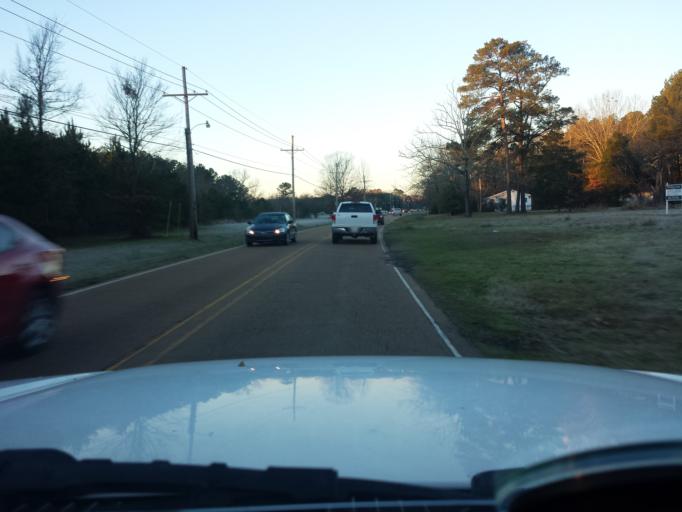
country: US
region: Mississippi
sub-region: Rankin County
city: Flowood
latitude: 32.3307
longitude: -90.0877
